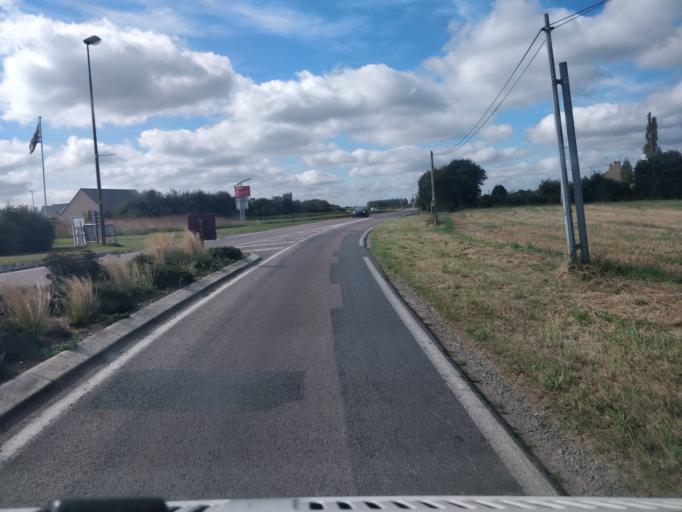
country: FR
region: Brittany
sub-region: Departement des Cotes-d'Armor
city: Plurien
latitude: 48.6242
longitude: -2.4098
